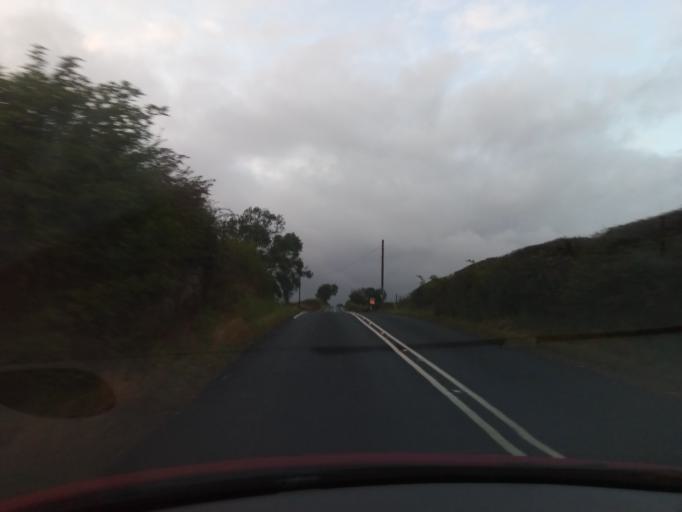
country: GB
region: England
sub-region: Darlington
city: Summerhouse
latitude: 54.5972
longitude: -1.6808
